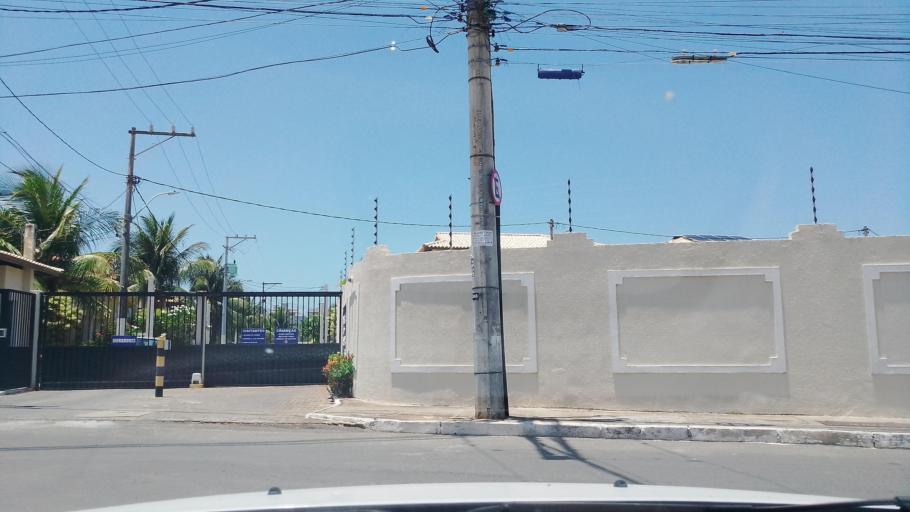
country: BR
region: Bahia
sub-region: Lauro De Freitas
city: Lauro de Freitas
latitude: -12.9378
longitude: -38.3302
